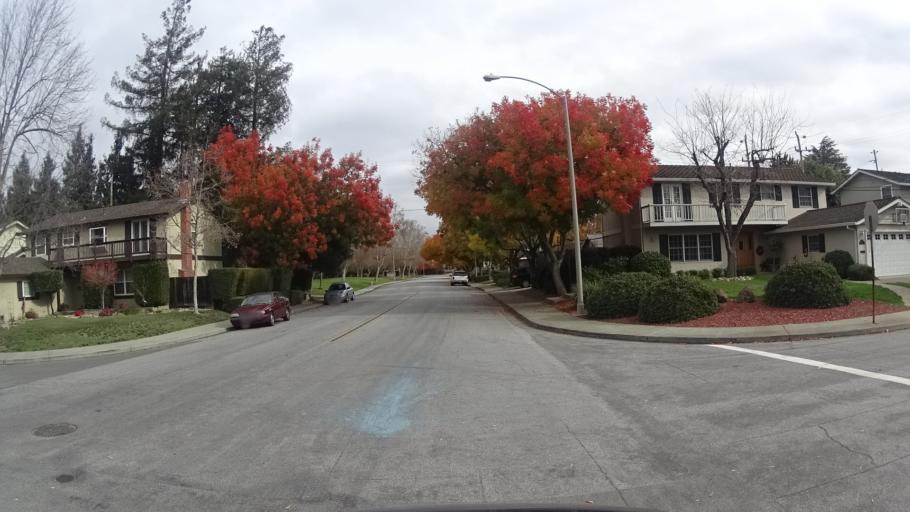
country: US
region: California
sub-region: Santa Clara County
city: Sunnyvale
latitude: 37.3622
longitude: -122.0398
